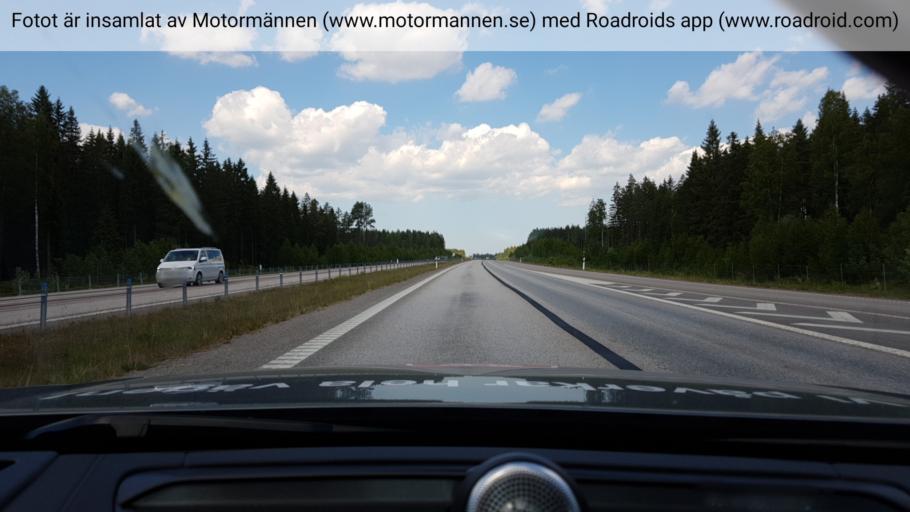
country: SE
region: Uppsala
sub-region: Tierps Kommun
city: Tierp
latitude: 60.2181
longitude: 17.4965
